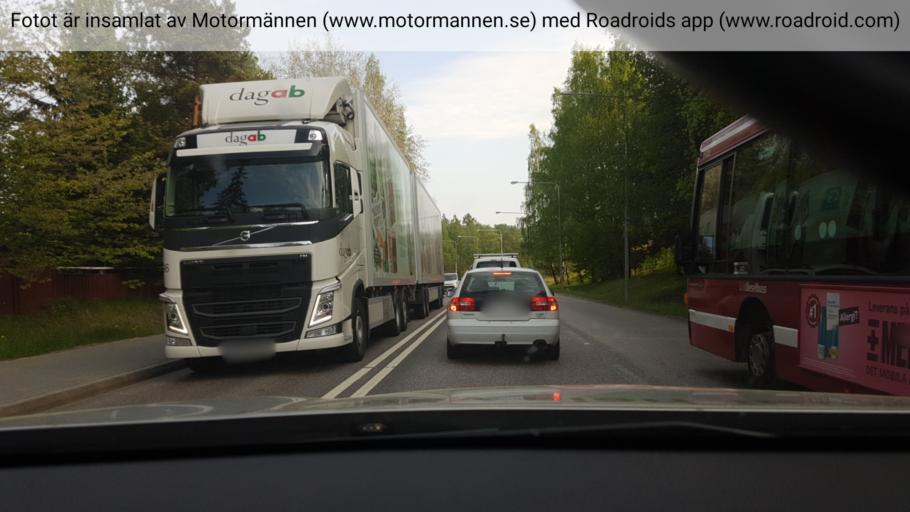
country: SE
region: Stockholm
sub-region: Tyreso Kommun
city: Bollmora
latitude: 59.2319
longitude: 18.1948
